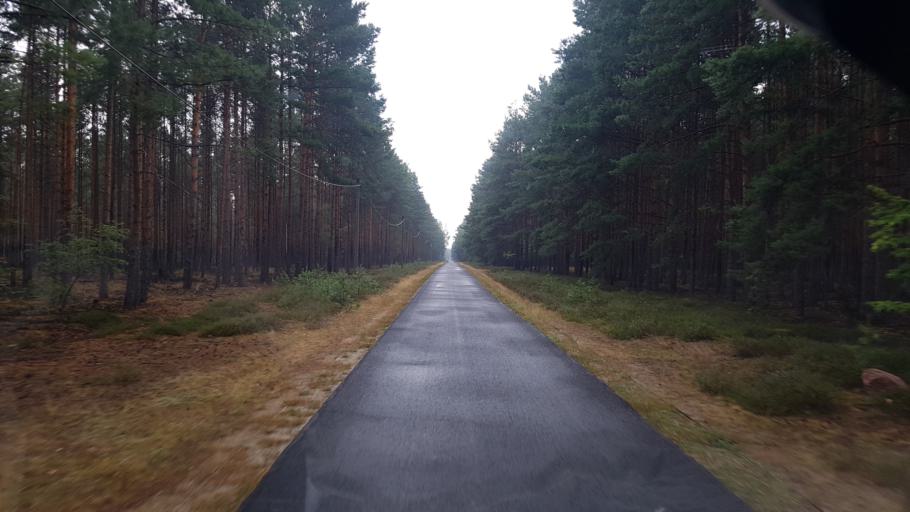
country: DE
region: Brandenburg
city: Finsterwalde
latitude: 51.6491
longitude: 13.7840
